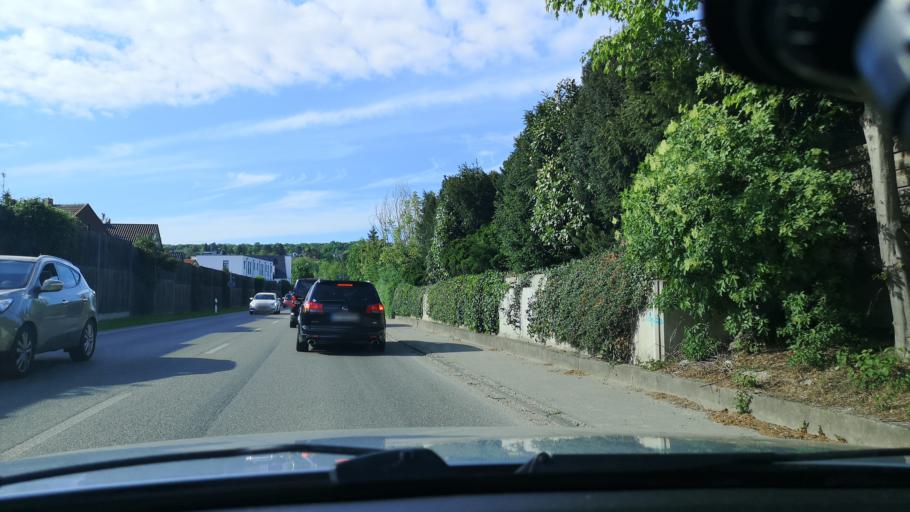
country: DE
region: Baden-Wuerttemberg
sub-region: Regierungsbezirk Stuttgart
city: Kirchheim unter Teck
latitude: 48.6508
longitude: 9.4611
